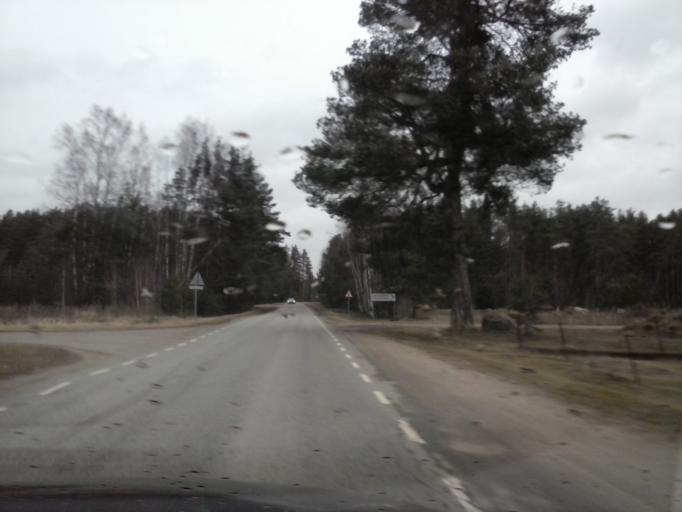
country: RU
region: Pskov
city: Pechory
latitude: 57.9611
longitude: 27.6295
